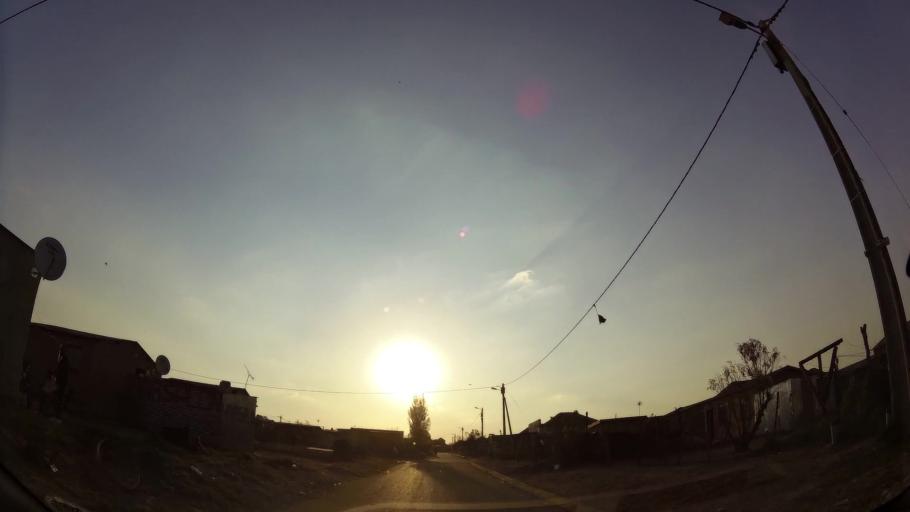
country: ZA
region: Gauteng
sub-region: Ekurhuleni Metropolitan Municipality
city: Benoni
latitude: -26.1542
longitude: 28.3834
